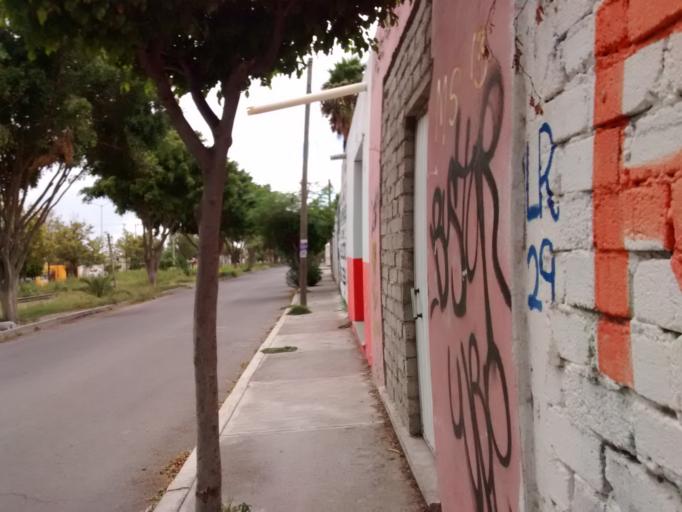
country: MX
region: Puebla
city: Tehuacan
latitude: 18.4703
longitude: -97.4052
